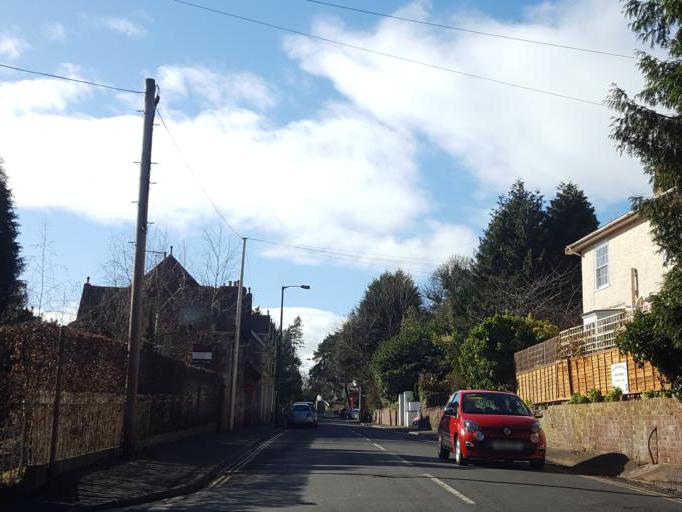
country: GB
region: England
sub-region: Worcestershire
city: Great Malvern
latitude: 52.0785
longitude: -2.3323
